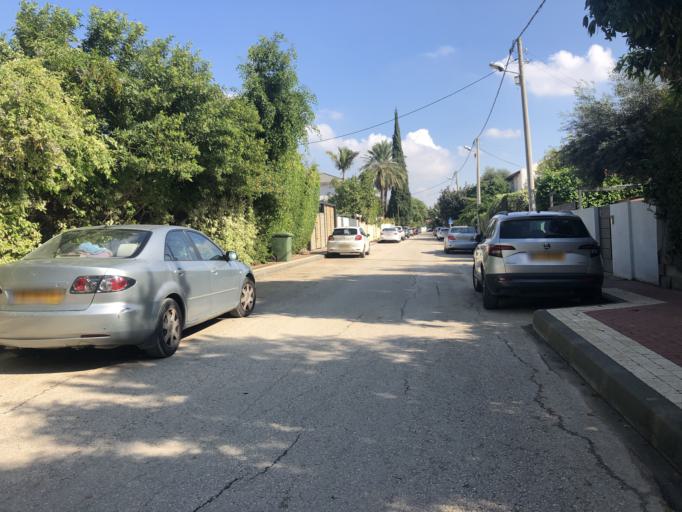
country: IL
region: Tel Aviv
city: Or Yehuda
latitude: 32.0273
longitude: 34.8748
